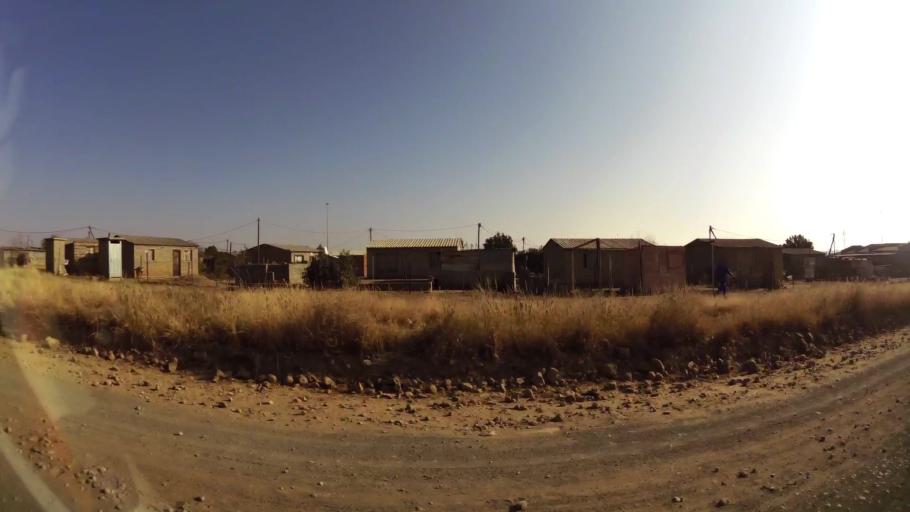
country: ZA
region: Orange Free State
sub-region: Mangaung Metropolitan Municipality
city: Bloemfontein
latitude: -29.2015
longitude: 26.2545
